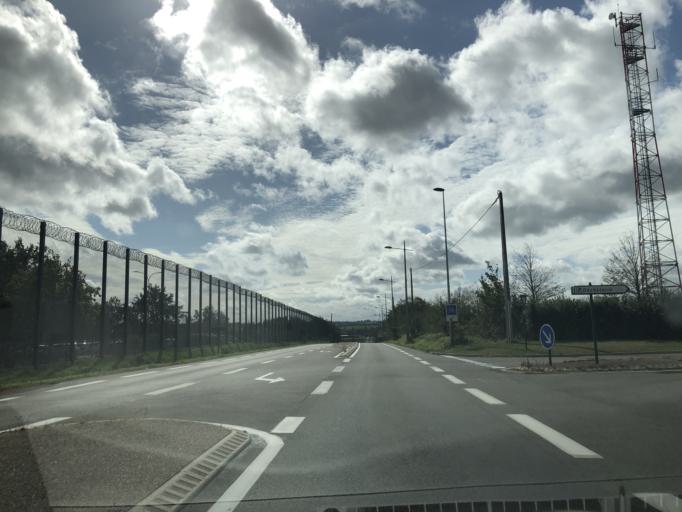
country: FR
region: Nord-Pas-de-Calais
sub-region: Departement du Pas-de-Calais
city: Longuenesse
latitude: 50.7265
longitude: 2.2457
